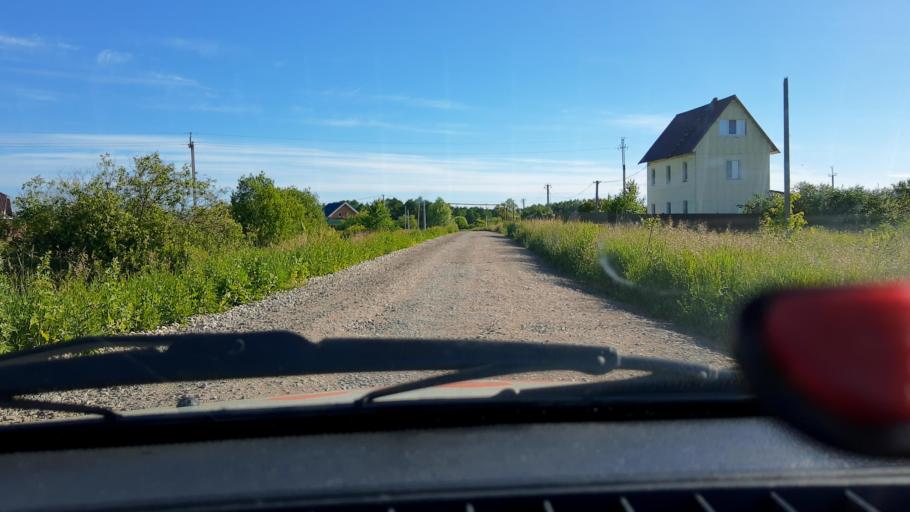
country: RU
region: Bashkortostan
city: Kabakovo
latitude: 54.7446
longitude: 56.2083
